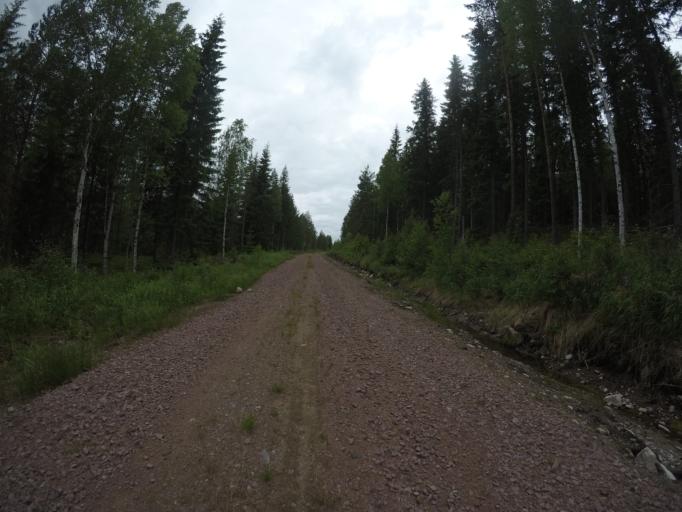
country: SE
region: Dalarna
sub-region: Ludvika Kommun
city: Abborrberget
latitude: 60.0943
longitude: 14.5097
